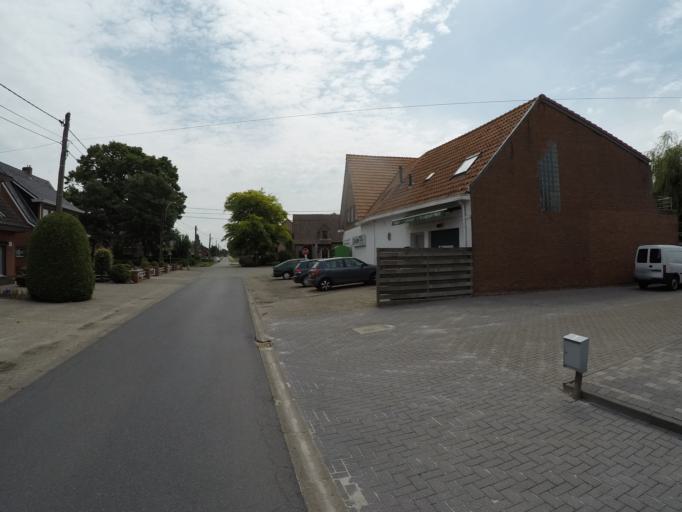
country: BE
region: Flanders
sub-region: Provincie Antwerpen
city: Essen
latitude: 51.4359
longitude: 4.5234
